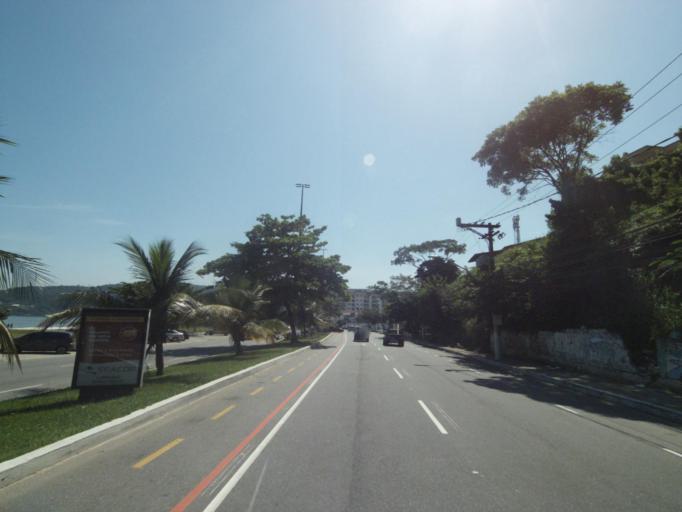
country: BR
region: Rio de Janeiro
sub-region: Niteroi
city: Niteroi
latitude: -22.9294
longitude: -43.0969
